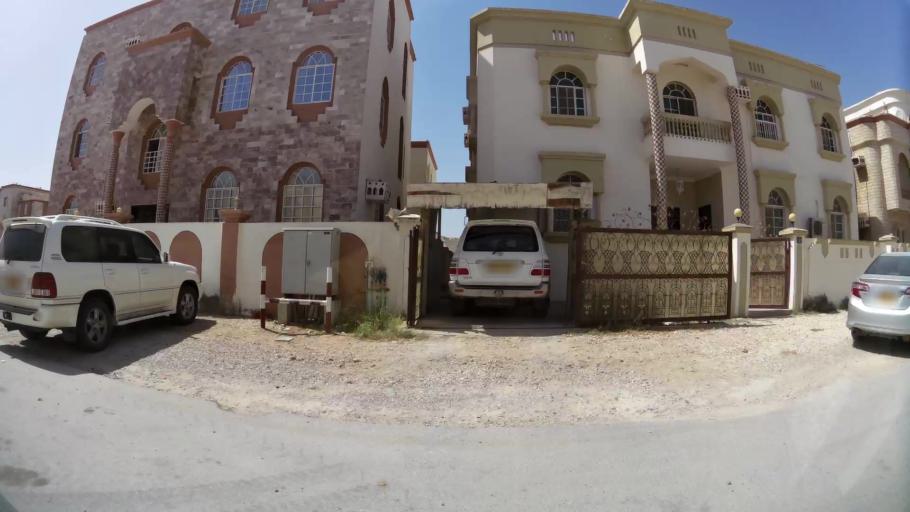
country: OM
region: Zufar
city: Salalah
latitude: 17.0400
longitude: 54.1554
